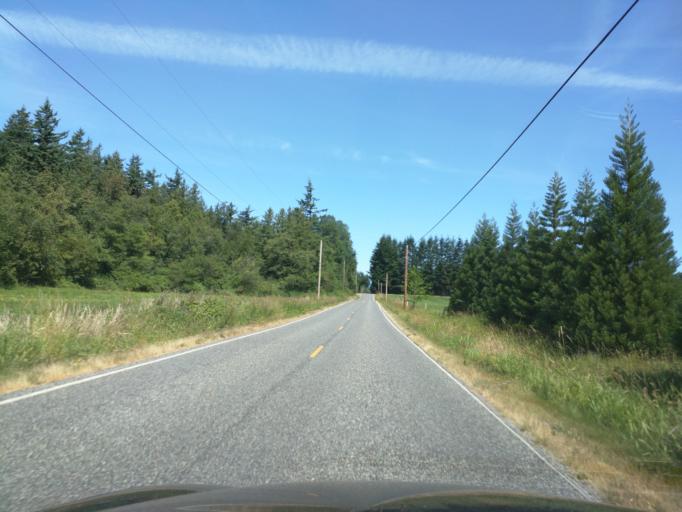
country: US
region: Washington
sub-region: Whatcom County
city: Everson
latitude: 48.8782
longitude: -122.3978
